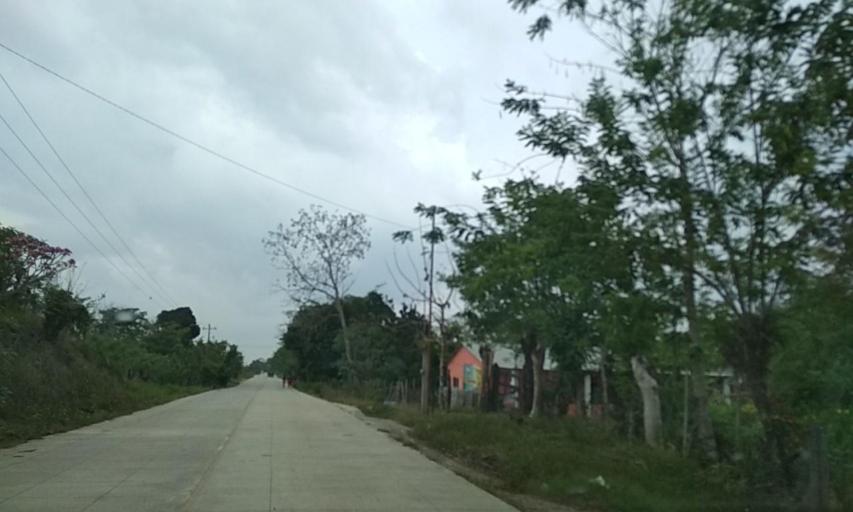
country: MX
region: Tabasco
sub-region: Huimanguillo
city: Francisco Rueda
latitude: 17.6599
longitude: -94.0919
